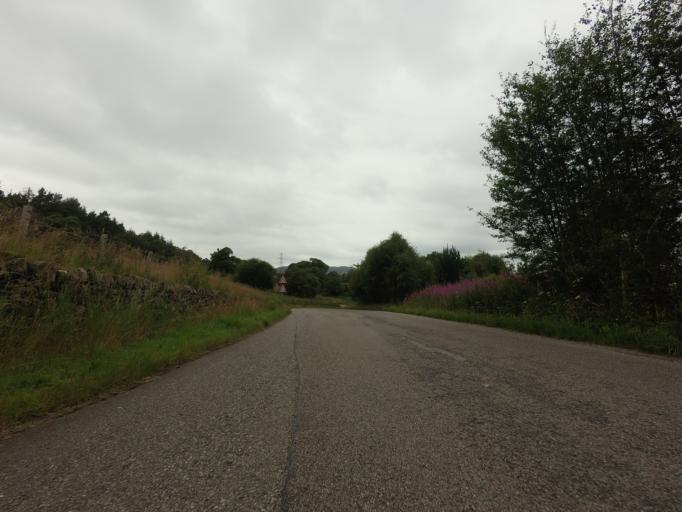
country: GB
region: Scotland
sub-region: Highland
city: Evanton
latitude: 57.9097
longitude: -4.3979
